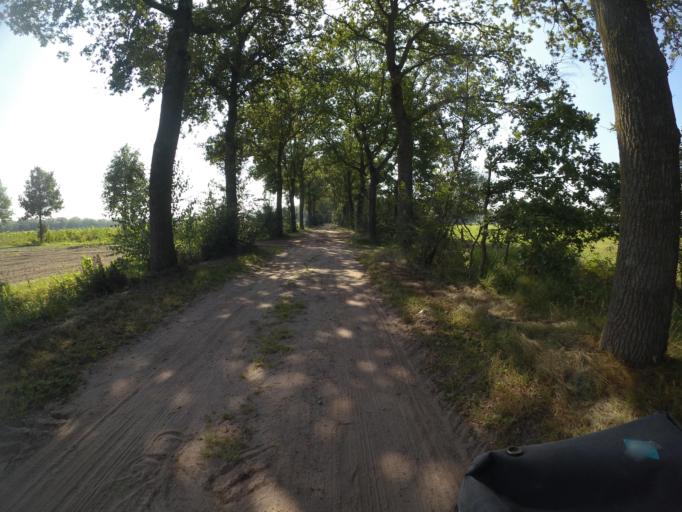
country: NL
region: North Brabant
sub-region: Gemeente Oirschot
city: Oirschot
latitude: 51.5447
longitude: 5.2770
